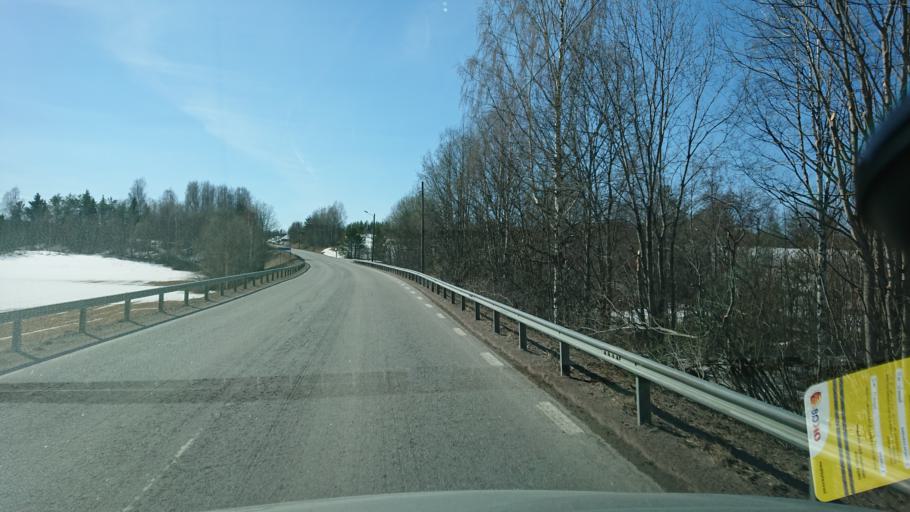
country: SE
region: Vaesternorrland
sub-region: Solleftea Kommun
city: As
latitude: 63.6493
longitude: 16.4601
